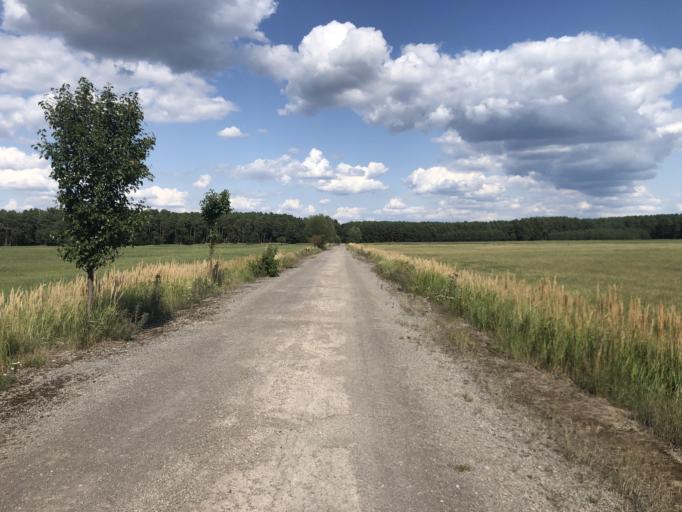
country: DE
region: Brandenburg
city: Mullrose
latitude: 52.2305
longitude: 14.3935
